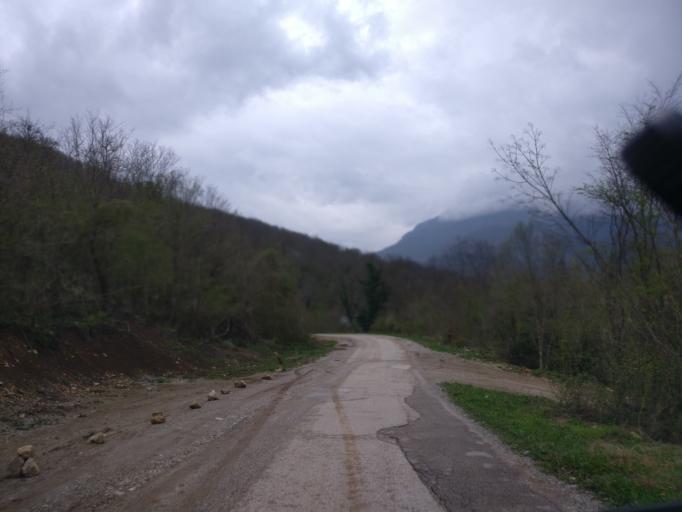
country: BA
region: Republika Srpska
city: Foca
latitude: 43.3544
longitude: 18.8207
